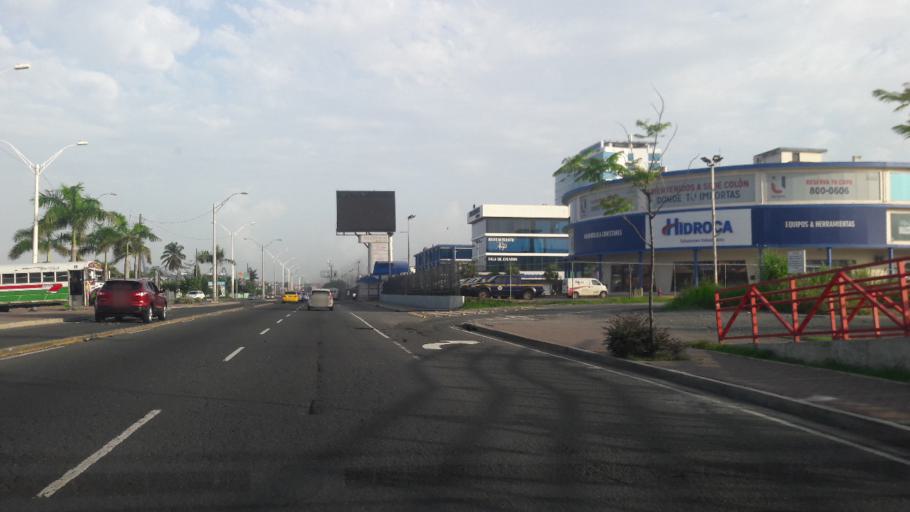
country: PA
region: Colon
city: Arco Iris
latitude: 9.3438
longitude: -79.8922
